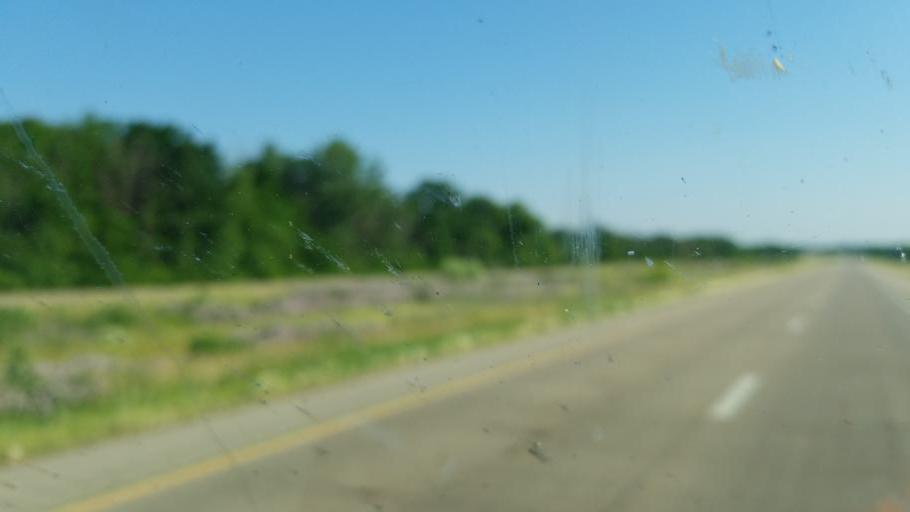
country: US
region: Illinois
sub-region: LaSalle County
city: Mendota
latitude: 41.4819
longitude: -89.0490
